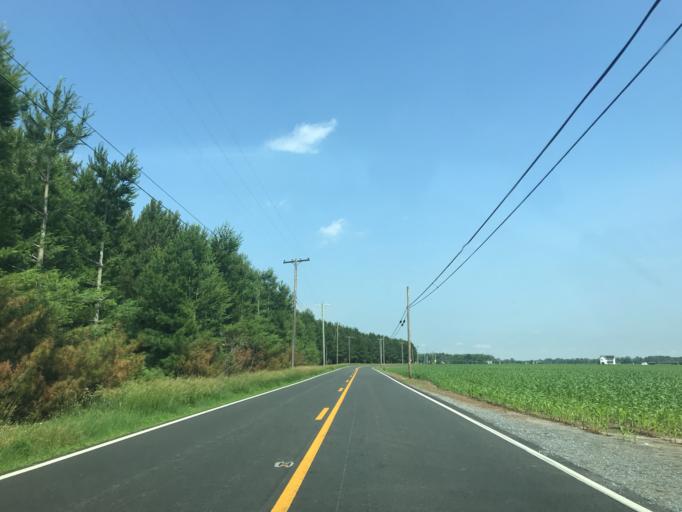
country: US
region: Maryland
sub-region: Dorchester County
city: Hurlock
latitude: 38.5758
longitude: -75.8232
